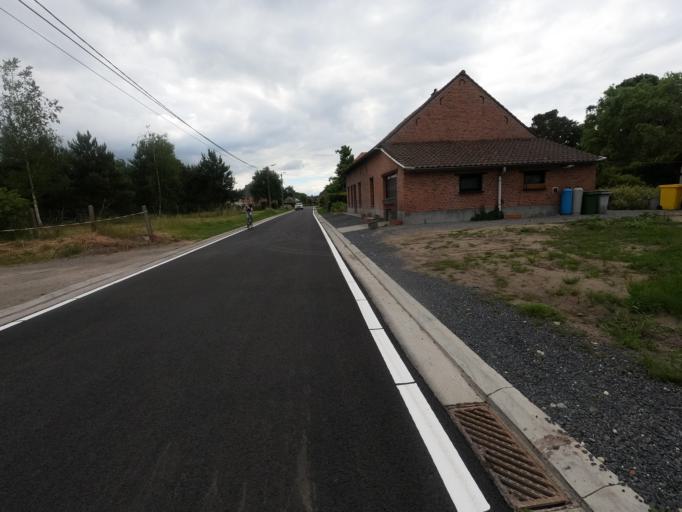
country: BE
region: Flanders
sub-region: Provincie Vlaams-Brabant
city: Tremelo
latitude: 51.0015
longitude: 4.7367
